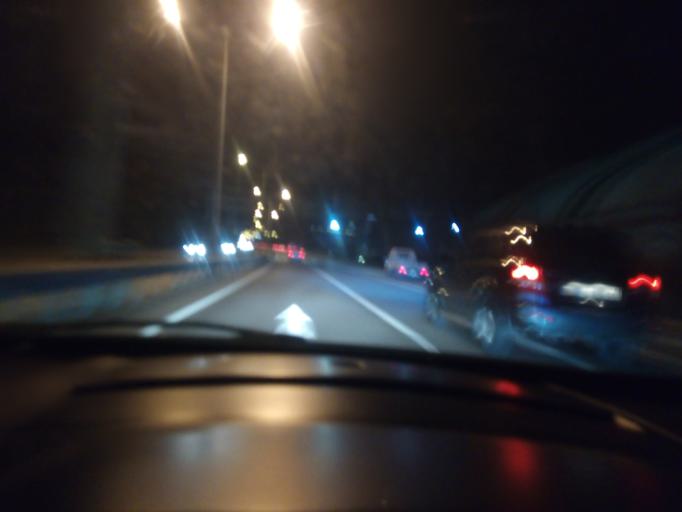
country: TR
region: Bursa
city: Niluefer
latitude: 40.3063
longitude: 28.9380
